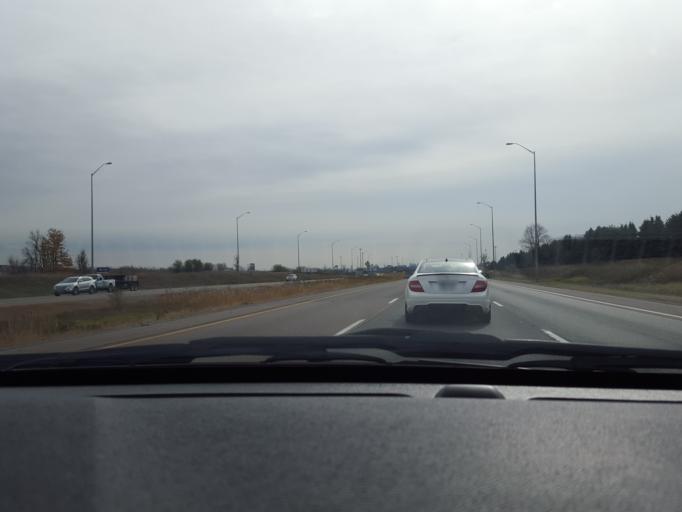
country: CA
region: Ontario
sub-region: York
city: Richmond Hill
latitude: 43.8915
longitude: -79.3817
